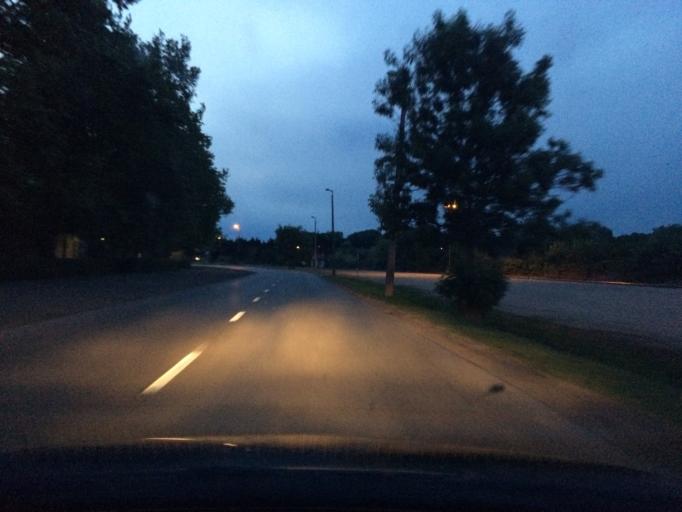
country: HU
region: Szabolcs-Szatmar-Bereg
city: Tiszavasvari
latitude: 47.9461
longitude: 21.3736
